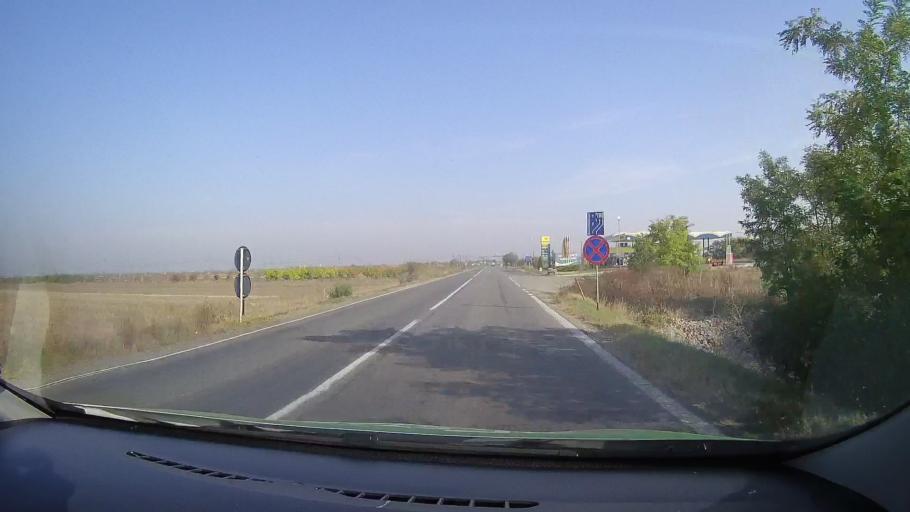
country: RO
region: Arad
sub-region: Comuna Pilu
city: Pilu
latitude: 46.6034
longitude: 21.3504
